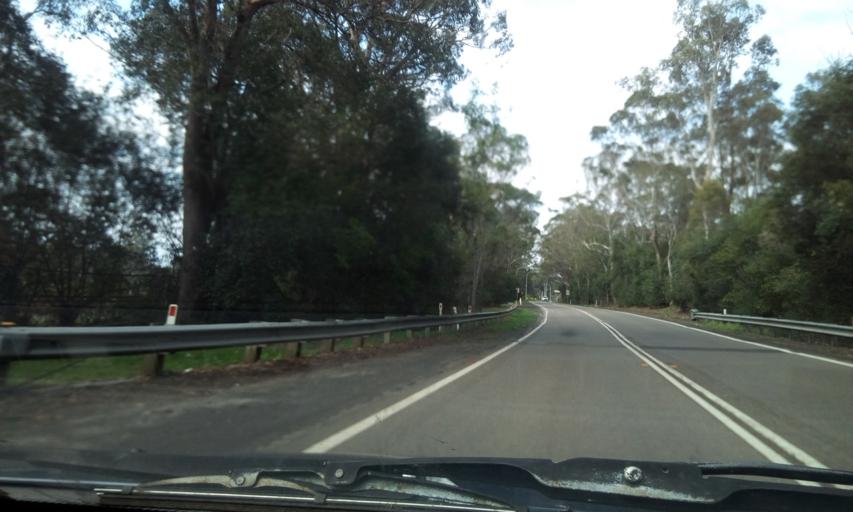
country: AU
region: New South Wales
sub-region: Campbelltown Municipality
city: Glen Alpine
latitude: -34.0803
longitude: 150.7809
